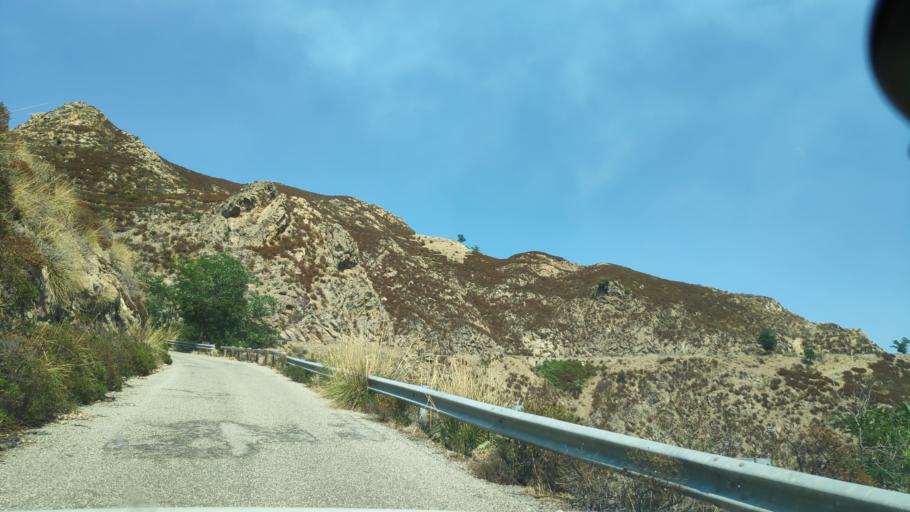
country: IT
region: Calabria
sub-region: Provincia di Reggio Calabria
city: Bova
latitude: 38.0007
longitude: 15.9250
